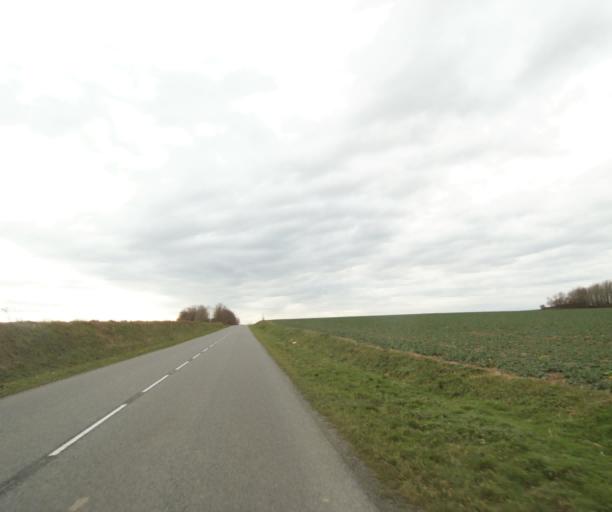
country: FR
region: Nord-Pas-de-Calais
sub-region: Departement du Nord
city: Sebourg
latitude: 50.3304
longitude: 3.6343
